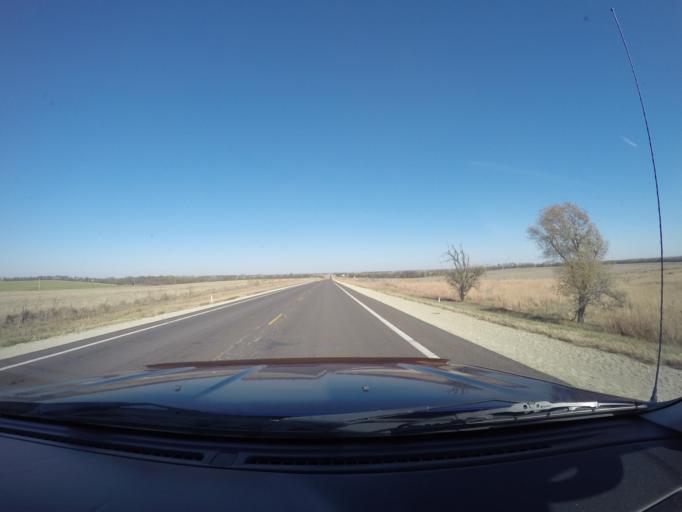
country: US
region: Kansas
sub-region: Marshall County
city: Blue Rapids
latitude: 39.6418
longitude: -96.7505
